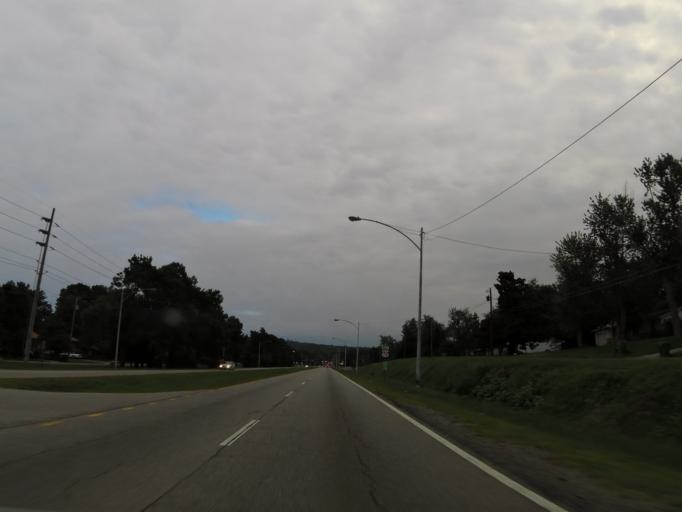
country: US
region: Alabama
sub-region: Madison County
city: Huntsville
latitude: 34.7617
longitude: -86.5852
